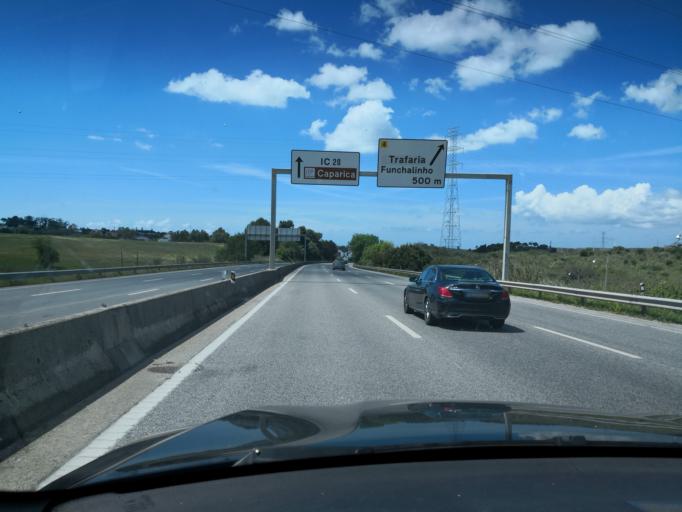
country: PT
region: Setubal
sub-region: Almada
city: Caparica
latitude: 38.6552
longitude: -9.2071
